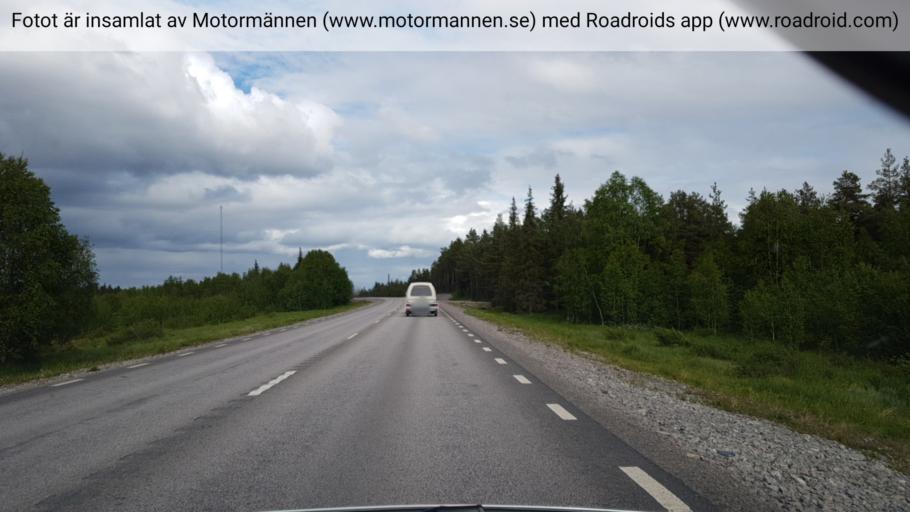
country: SE
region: Norrbotten
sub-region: Gallivare Kommun
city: Malmberget
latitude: 67.6649
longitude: 21.5907
